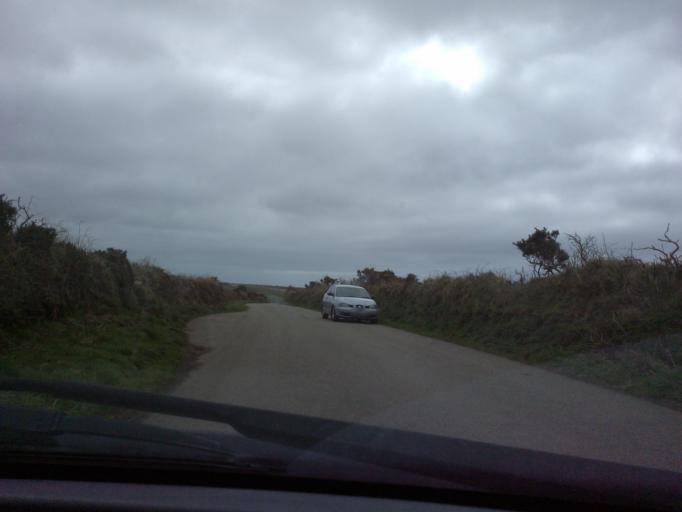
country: GB
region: England
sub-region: Cornwall
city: Penzance
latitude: 50.1473
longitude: -5.5998
